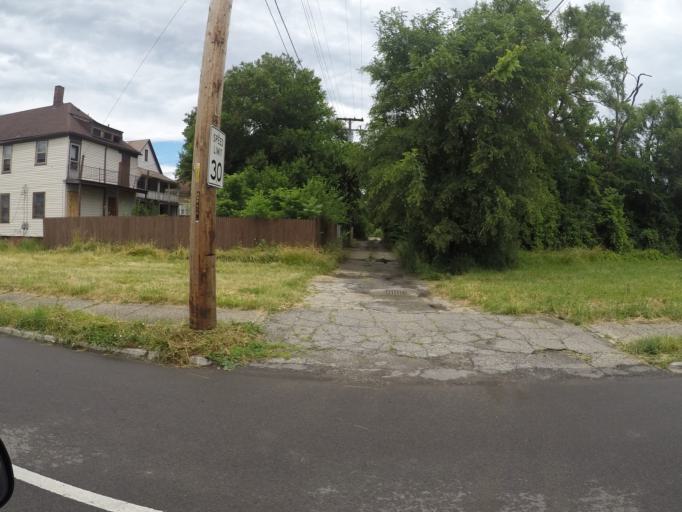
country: US
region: Michigan
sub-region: Wayne County
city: Hamtramck
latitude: 42.3759
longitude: -83.0132
